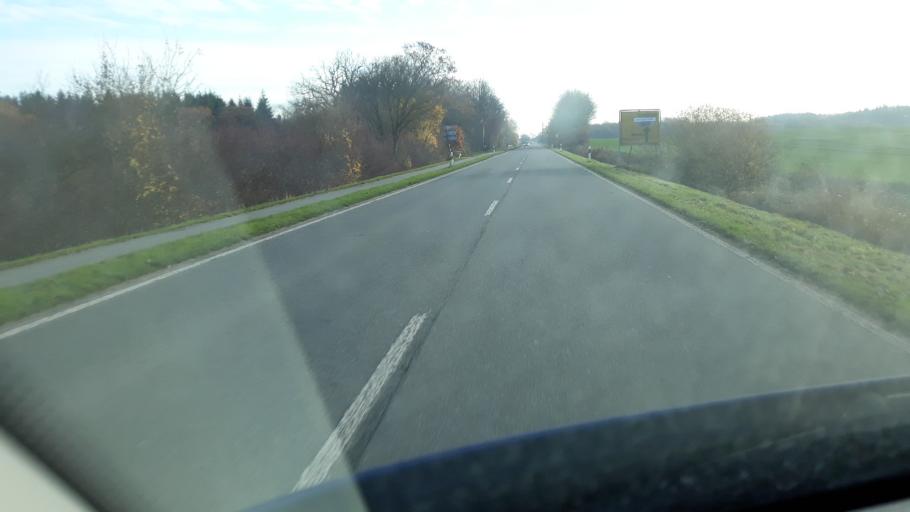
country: DE
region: Schleswig-Holstein
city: Maasholm
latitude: 54.6619
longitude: 9.9859
